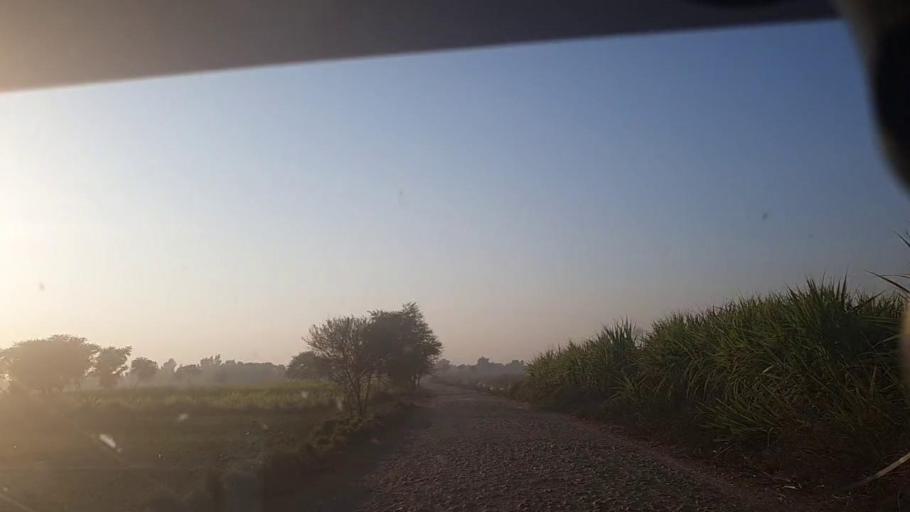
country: PK
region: Sindh
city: Sobhadero
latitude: 27.3610
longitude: 68.4197
